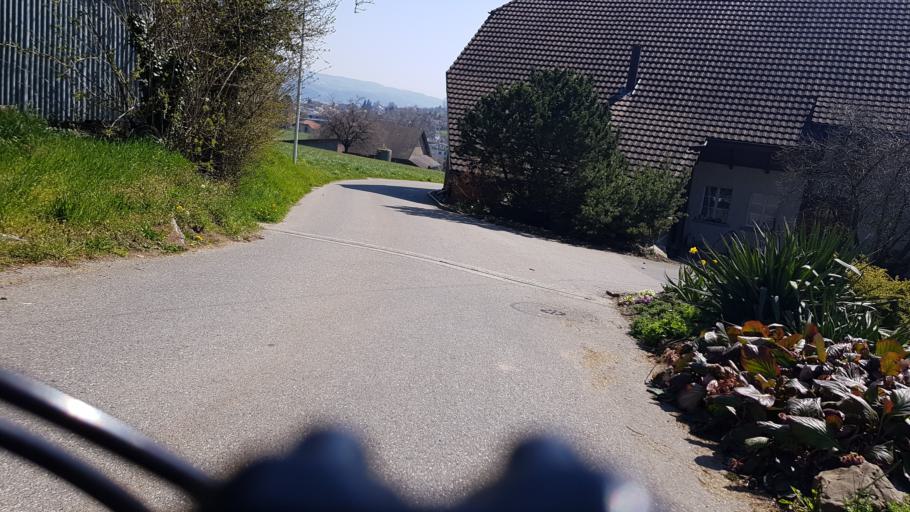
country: CH
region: Aargau
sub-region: Bezirk Kulm
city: Reinach
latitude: 47.2673
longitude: 8.1885
